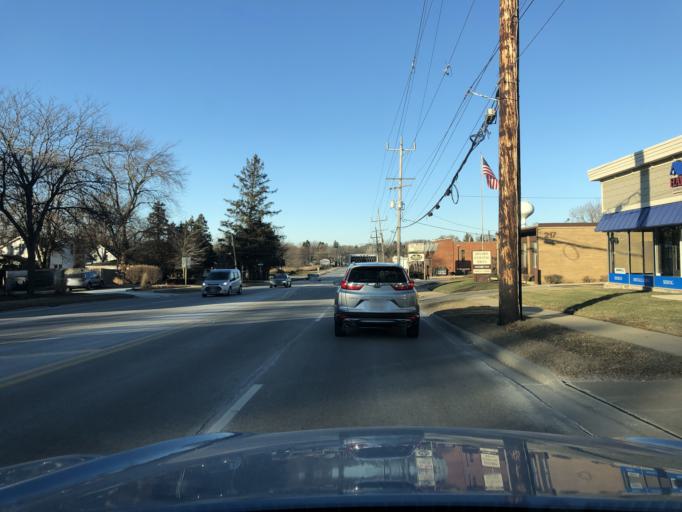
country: US
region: Illinois
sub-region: Cook County
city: Barrington
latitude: 42.1555
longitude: -88.1282
